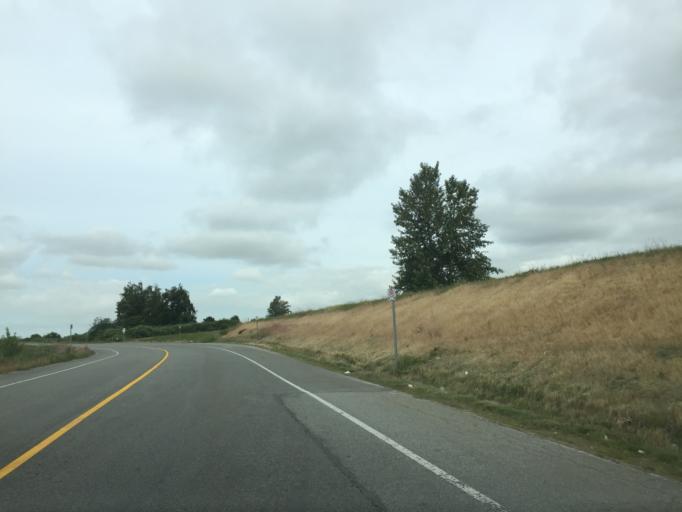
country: CA
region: British Columbia
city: Richmond
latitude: 49.1991
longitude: -123.1411
